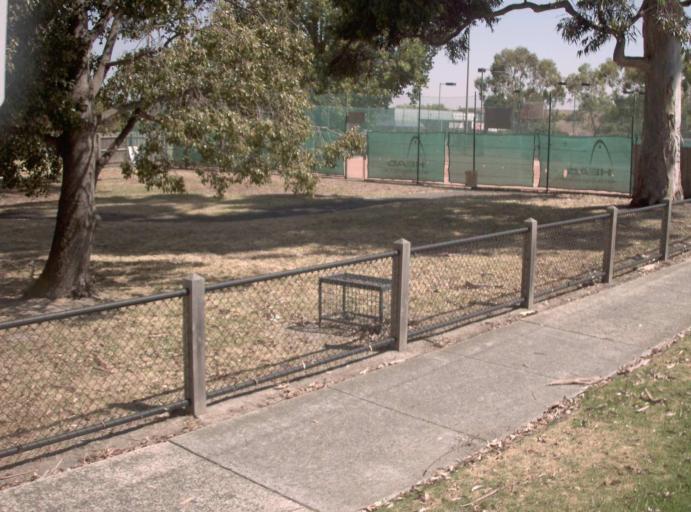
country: AU
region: Victoria
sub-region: Monash
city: Ashwood
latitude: -37.8544
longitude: 145.0949
